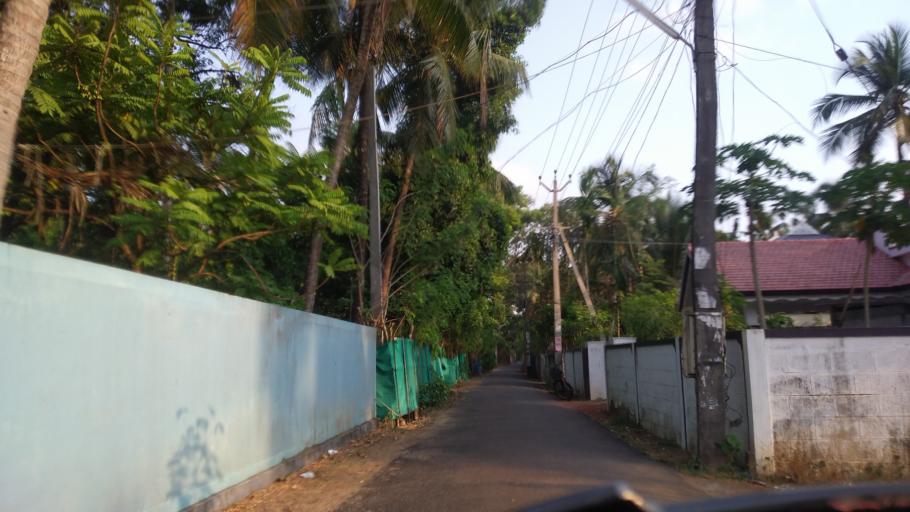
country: IN
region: Kerala
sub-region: Thrissur District
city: Thanniyam
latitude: 10.4169
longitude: 76.0864
